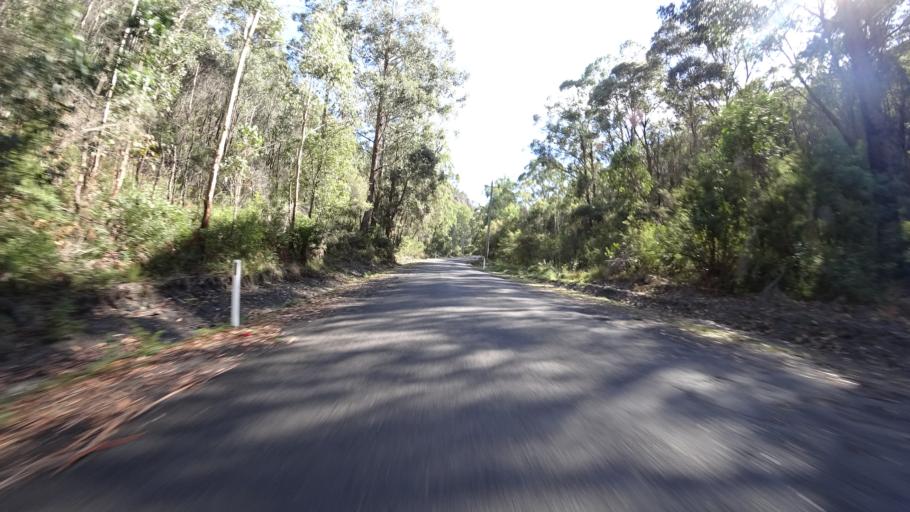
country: AU
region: New South Wales
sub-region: Lithgow
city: Lithgow
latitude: -33.4545
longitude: 150.1737
